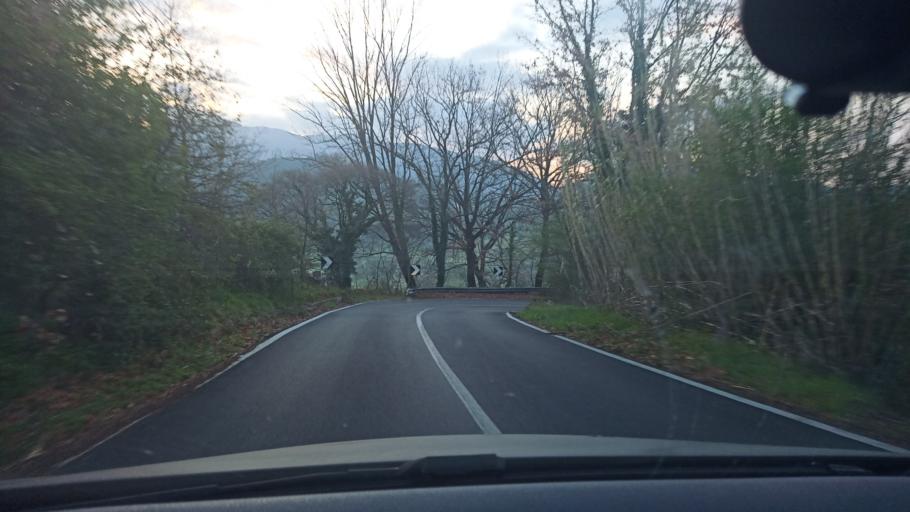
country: IT
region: Latium
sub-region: Provincia di Rieti
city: Torri in Sabina
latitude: 42.3291
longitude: 12.6461
